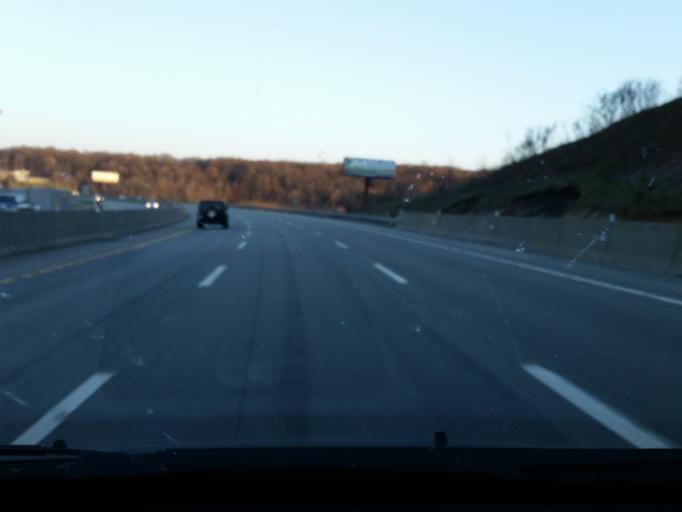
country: US
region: Pennsylvania
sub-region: Fayette County
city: Bear Rocks
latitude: 40.1176
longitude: -79.3976
